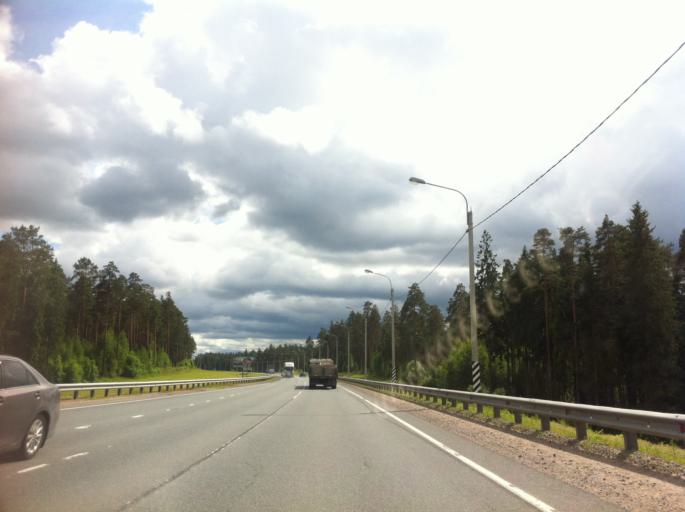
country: RU
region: Leningrad
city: Luga
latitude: 58.7246
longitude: 29.8782
